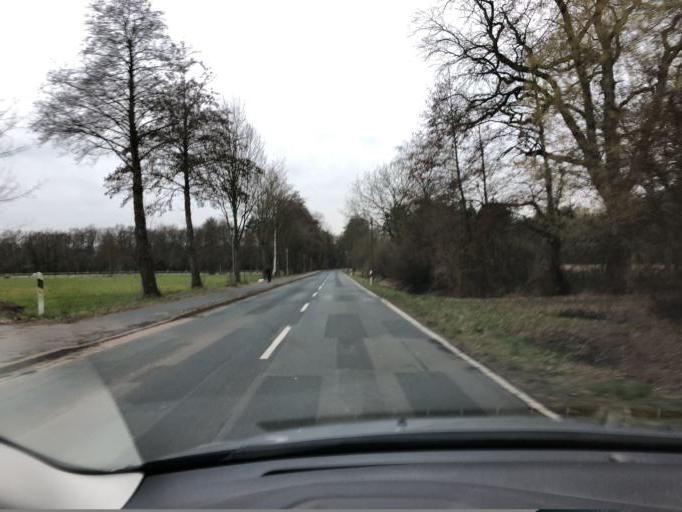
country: DE
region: Lower Saxony
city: Ganderkesee
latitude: 53.0803
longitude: 8.5705
